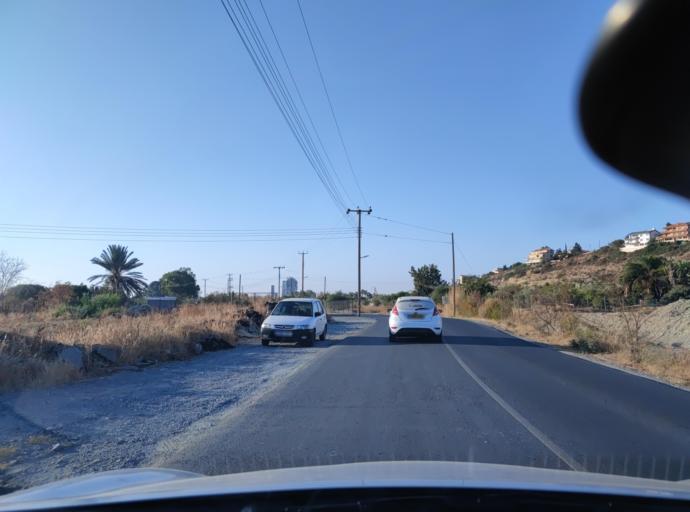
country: CY
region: Limassol
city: Mouttagiaka
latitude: 34.7154
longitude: 33.0888
